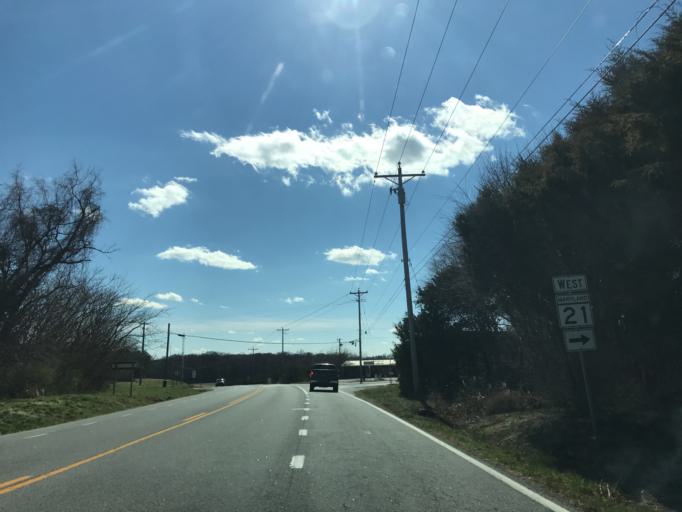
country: US
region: Maryland
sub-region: Kent County
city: Rock Hall
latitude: 39.1990
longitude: -76.1894
